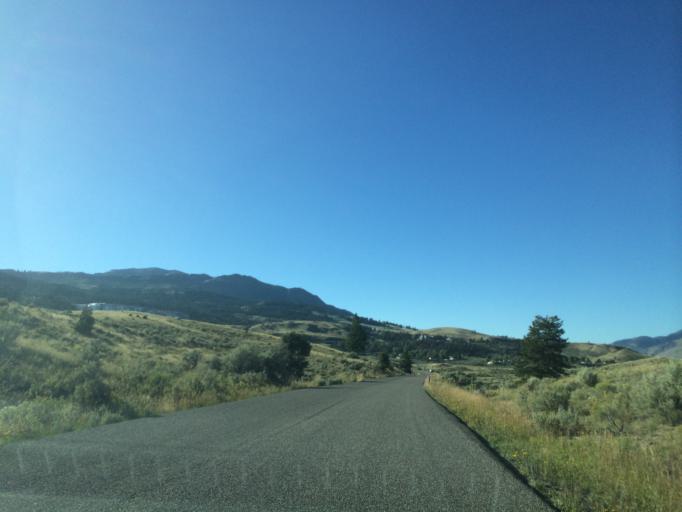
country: US
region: Montana
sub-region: Gallatin County
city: West Yellowstone
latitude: 44.9616
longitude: -110.6840
